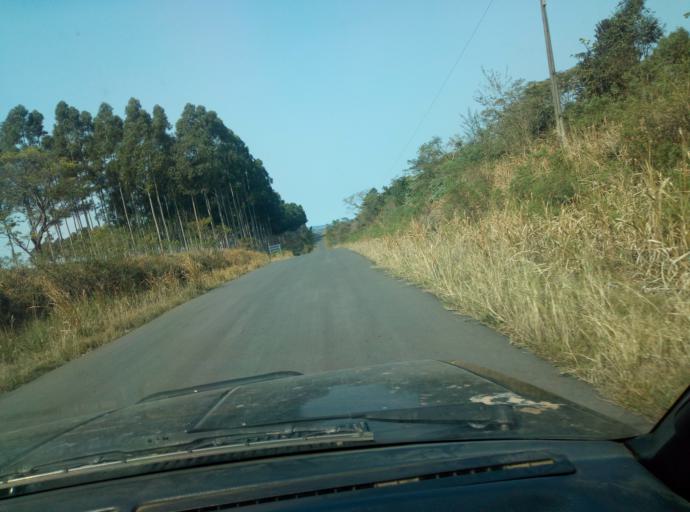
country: PY
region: Caaguazu
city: Carayao
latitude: -25.2449
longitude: -56.2881
